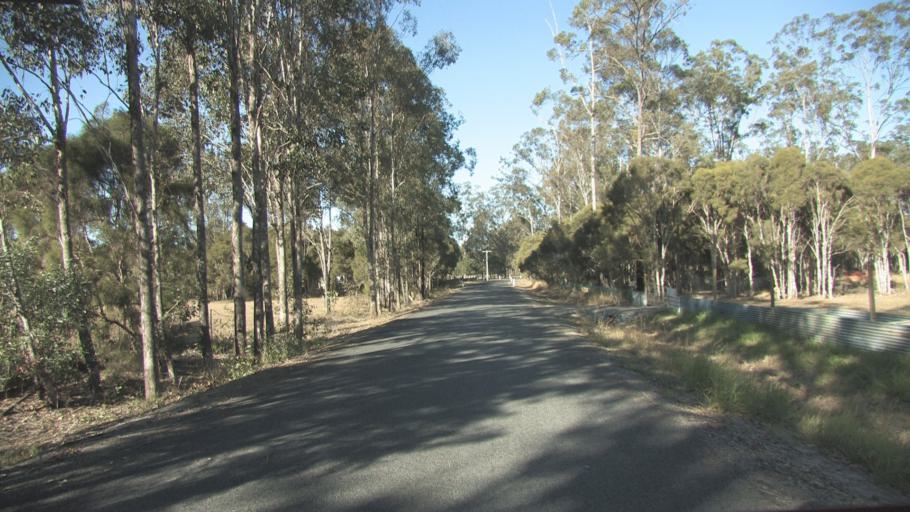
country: AU
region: Queensland
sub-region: Logan
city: Cedar Vale
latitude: -27.8403
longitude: 153.0026
